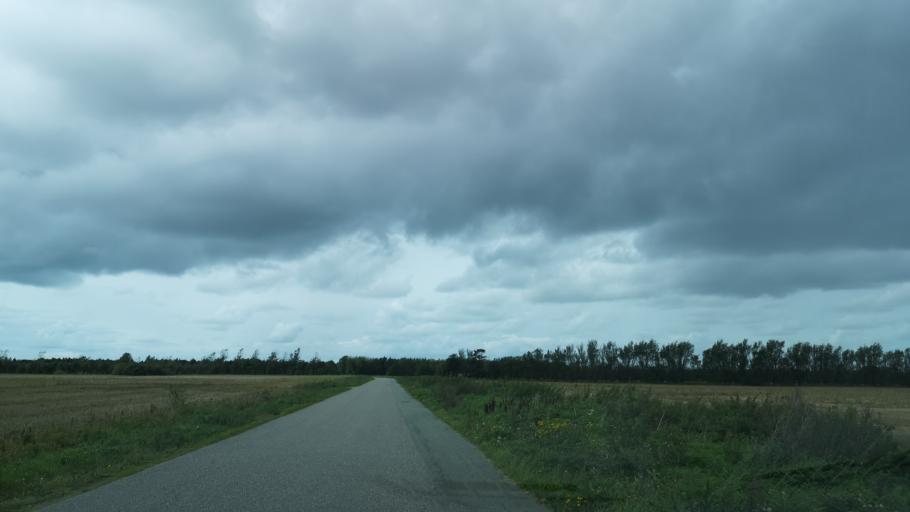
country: DK
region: South Denmark
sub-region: Varde Kommune
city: Oksbol
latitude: 55.8379
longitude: 8.2978
